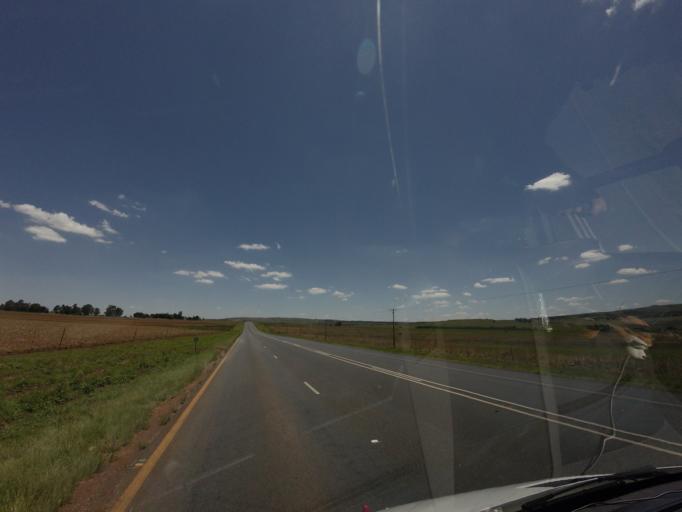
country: ZA
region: Mpumalanga
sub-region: Nkangala District Municipality
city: Belfast
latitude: -25.7003
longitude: 30.1960
